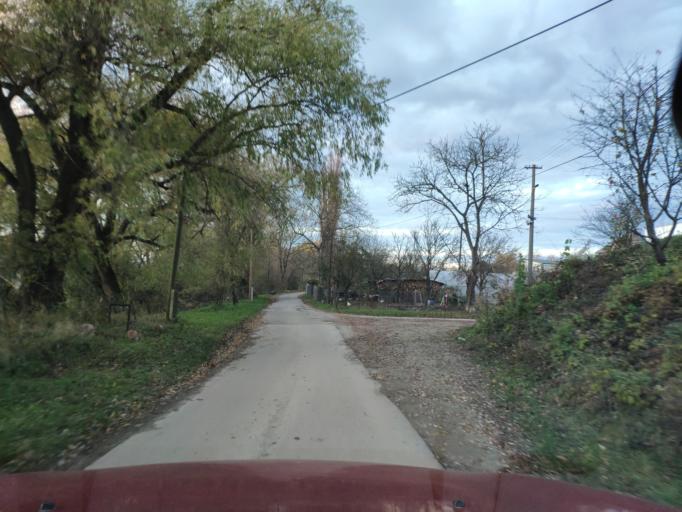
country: SK
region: Kosicky
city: Kosice
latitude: 48.6589
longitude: 21.3563
